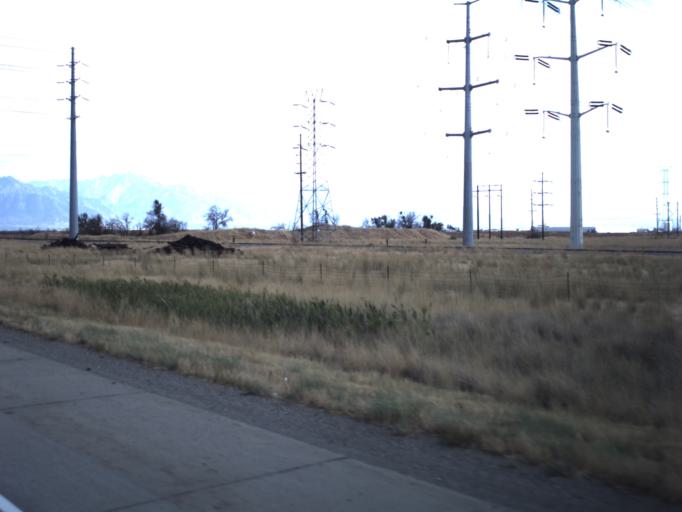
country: US
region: Utah
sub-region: Salt Lake County
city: West Valley City
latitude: 40.7700
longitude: -112.0073
